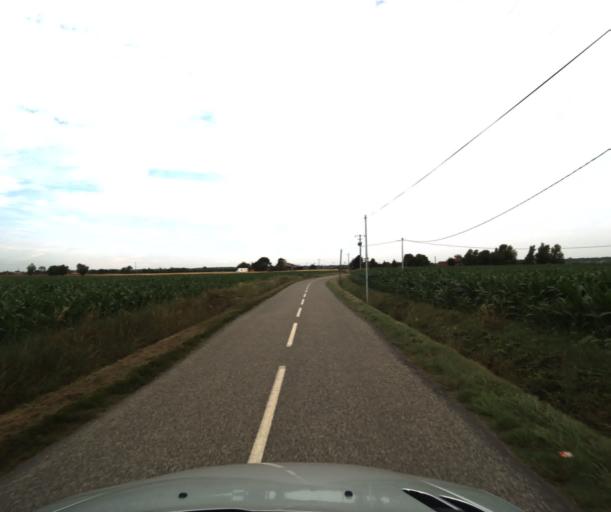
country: FR
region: Midi-Pyrenees
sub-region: Departement de la Haute-Garonne
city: Lacasse
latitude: 43.4252
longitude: 1.2584
